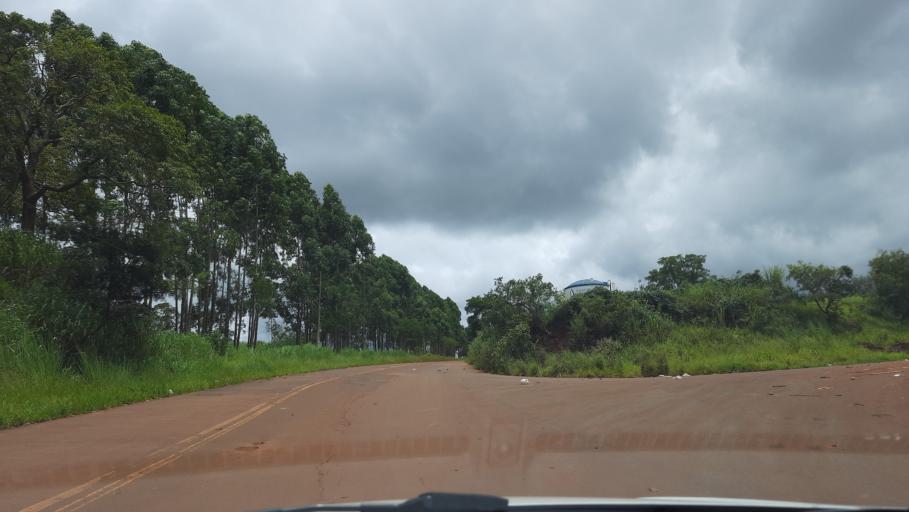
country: BR
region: Sao Paulo
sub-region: Casa Branca
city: Casa Branca
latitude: -21.7891
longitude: -47.0971
